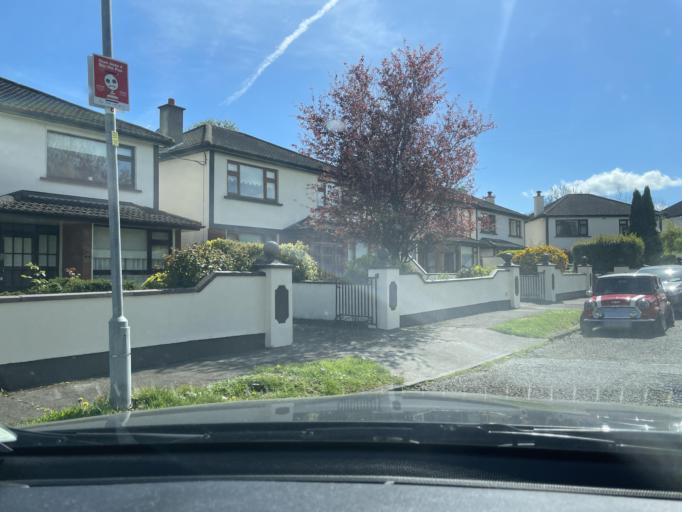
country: IE
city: Killester
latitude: 53.3747
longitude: -6.1921
